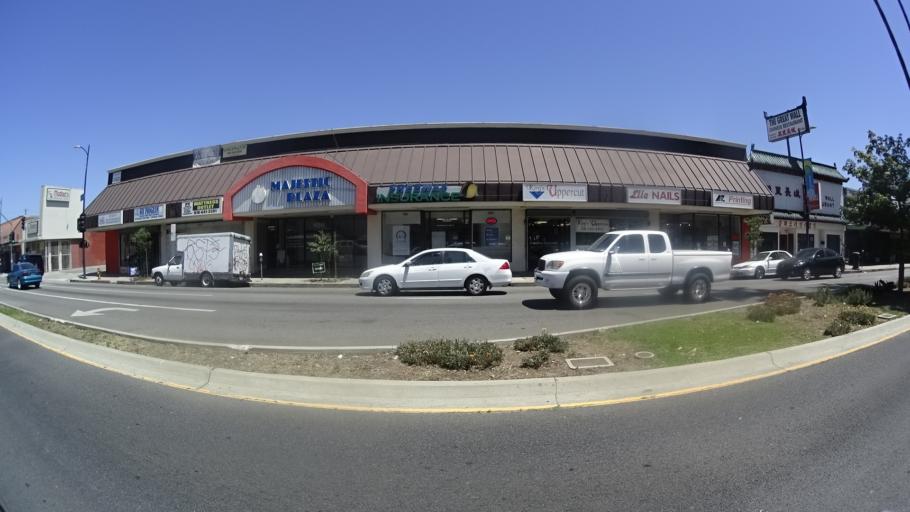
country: US
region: California
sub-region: Los Angeles County
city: Northridge
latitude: 34.2009
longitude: -118.5332
